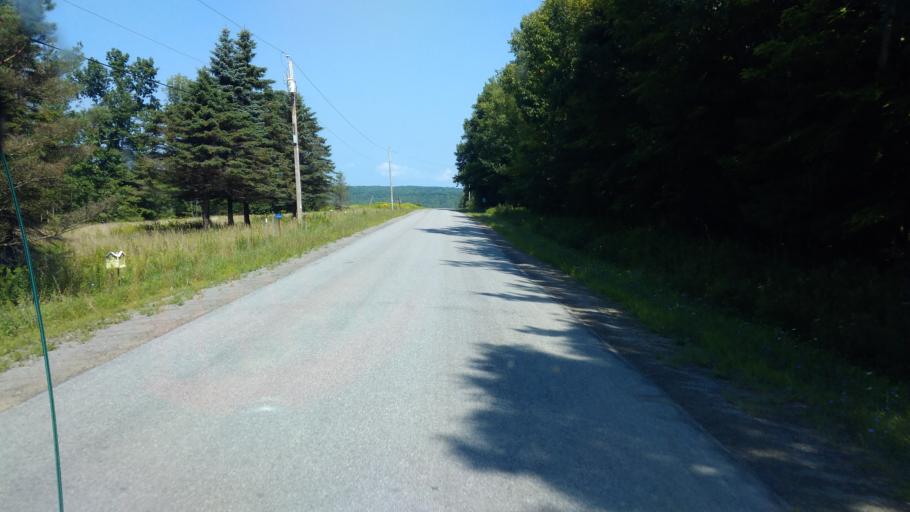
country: US
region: New York
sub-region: Allegany County
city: Belmont
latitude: 42.3353
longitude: -78.0741
